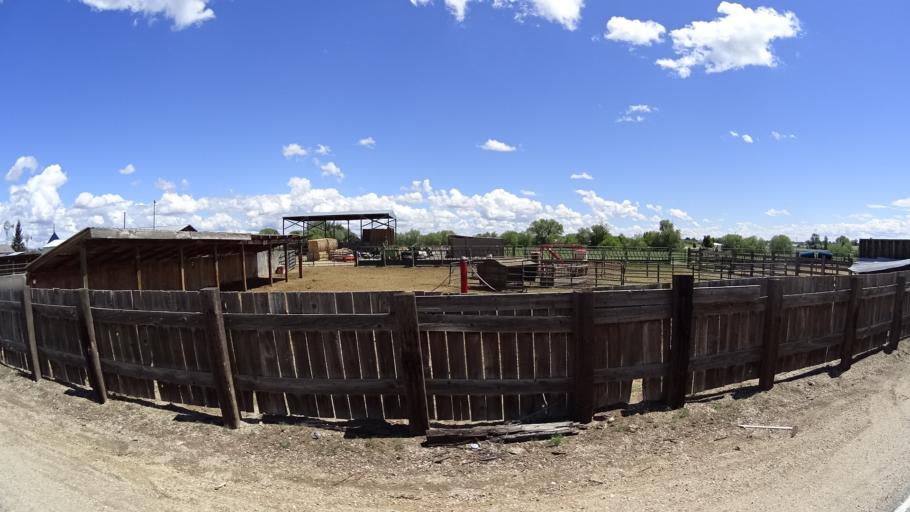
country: US
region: Idaho
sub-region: Ada County
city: Kuna
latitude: 43.5597
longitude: -116.4737
